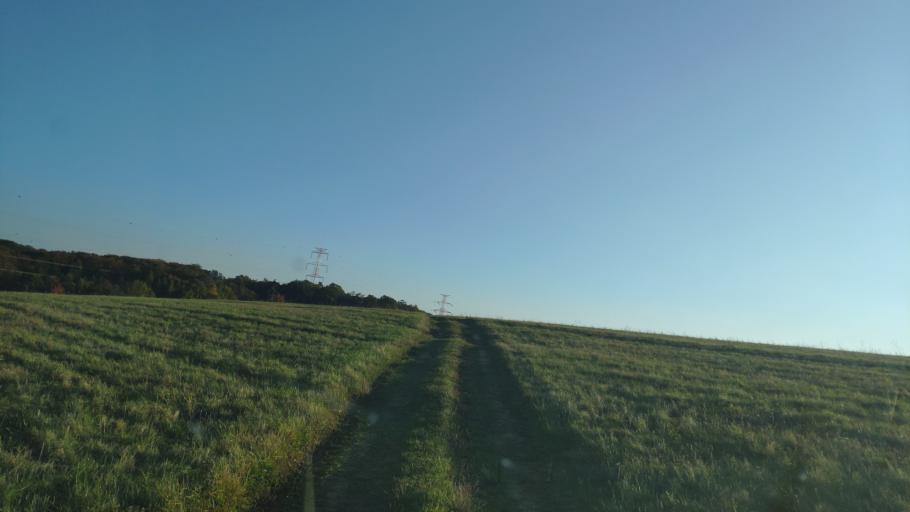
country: SK
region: Kosicky
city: Kosice
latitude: 48.7130
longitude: 21.1687
